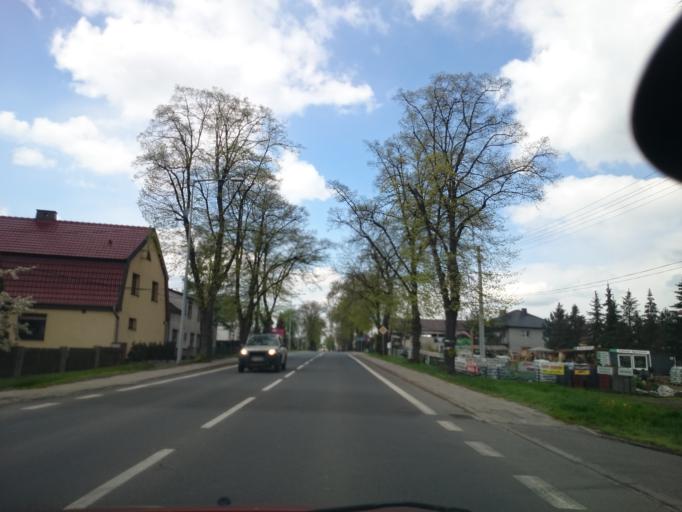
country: PL
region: Opole Voivodeship
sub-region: Powiat opolski
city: Opole
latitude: 50.6467
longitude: 17.9822
